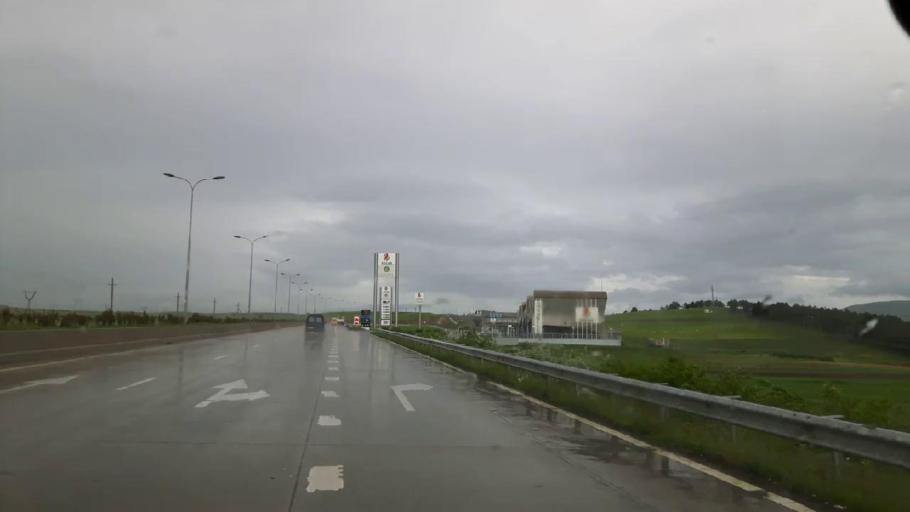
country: GE
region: Shida Kartli
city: Gori
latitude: 42.0169
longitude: 44.0254
